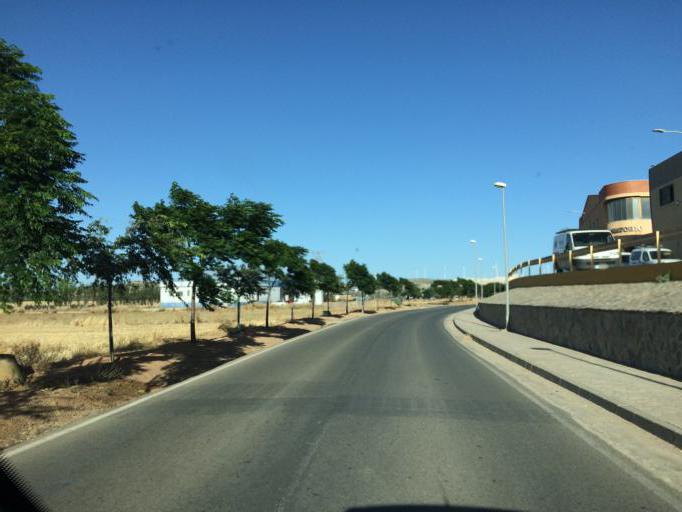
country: ES
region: Andalusia
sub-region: Provincia de Malaga
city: Campillos
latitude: 37.0490
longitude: -4.8725
